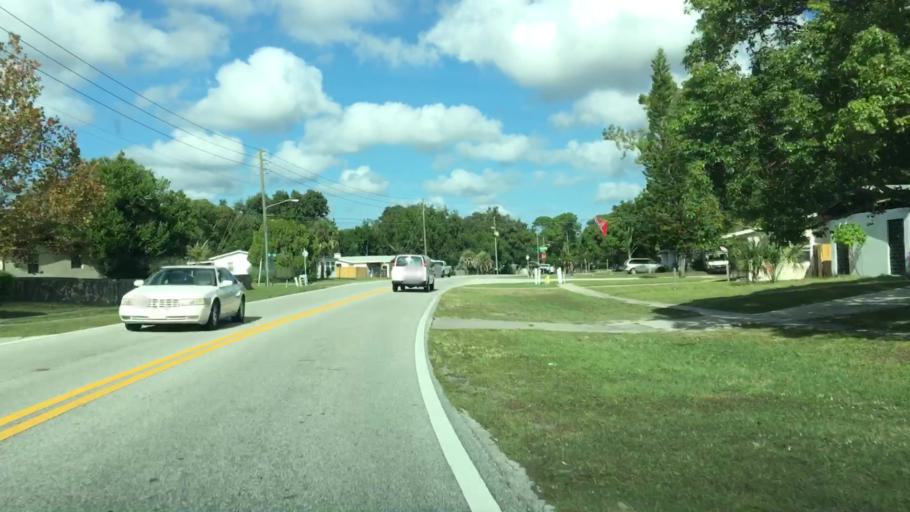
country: US
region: Florida
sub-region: Volusia County
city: Deltona
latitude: 28.8980
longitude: -81.2616
